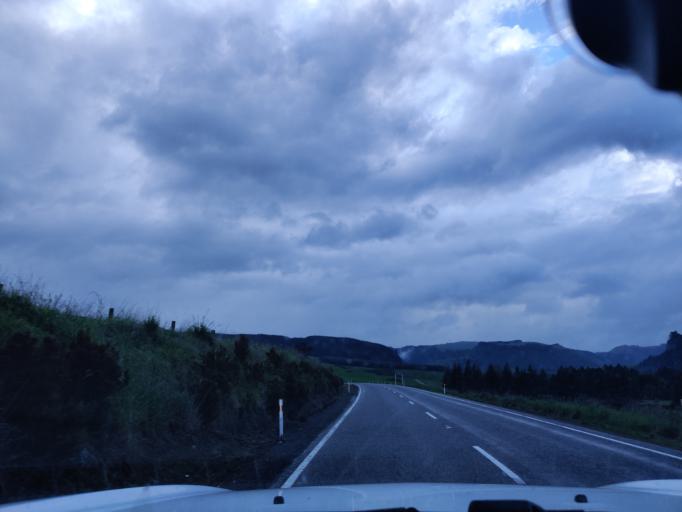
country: NZ
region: Waikato
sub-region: South Waikato District
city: Tokoroa
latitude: -38.4143
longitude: 175.8073
